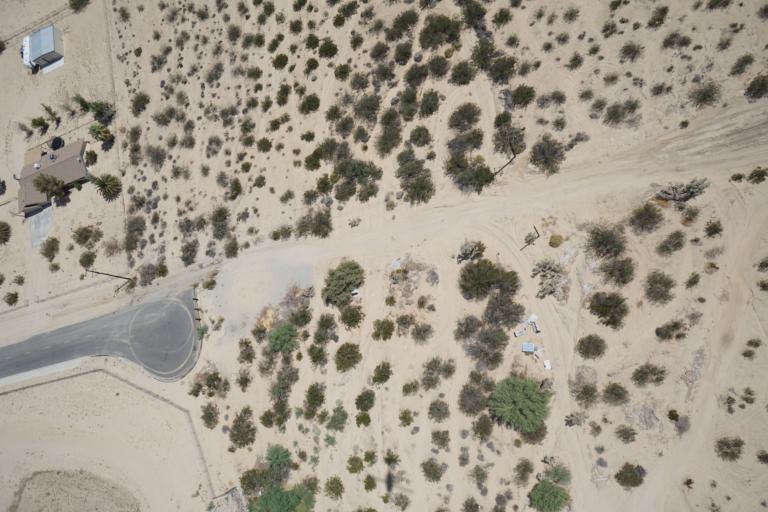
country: US
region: California
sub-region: San Bernardino County
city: Twentynine Palms
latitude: 34.1439
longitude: -116.0457
